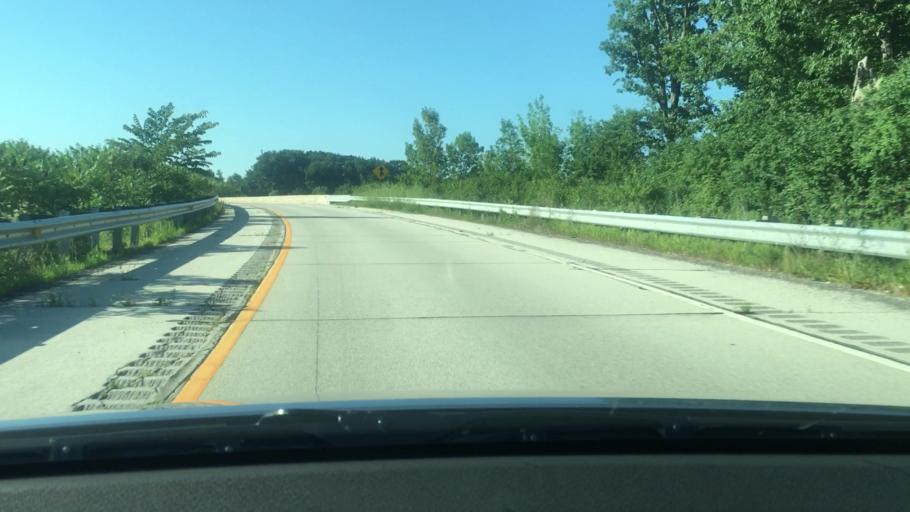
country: US
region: Wisconsin
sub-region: Brown County
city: Ashwaubenon
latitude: 44.4817
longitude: -88.0774
